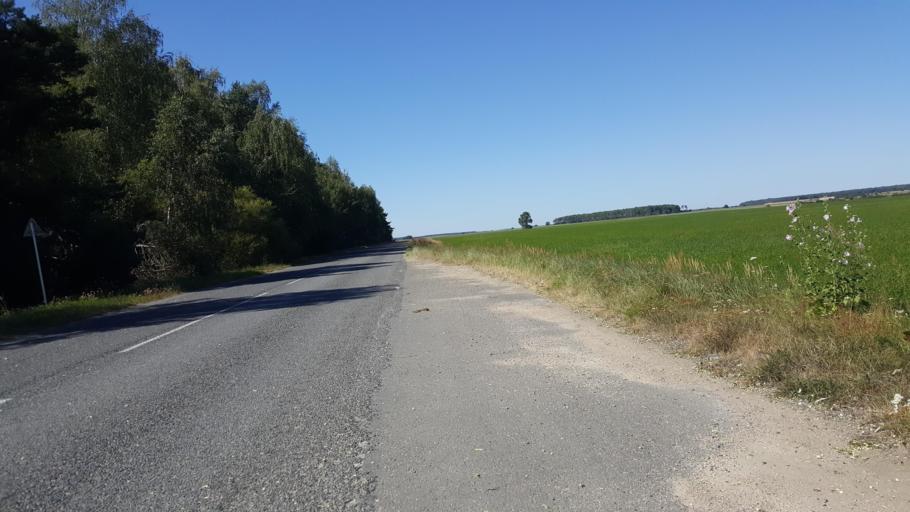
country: PL
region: Lublin Voivodeship
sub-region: Powiat bialski
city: Rokitno
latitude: 52.2234
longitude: 23.3970
